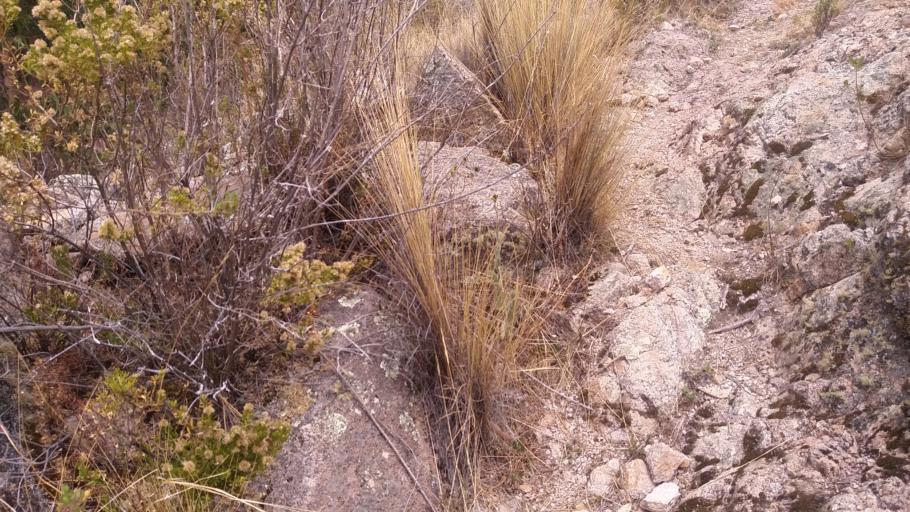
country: PE
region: Puno
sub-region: Yunguyo
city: Yunguyo
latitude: -16.1845
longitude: -69.0843
